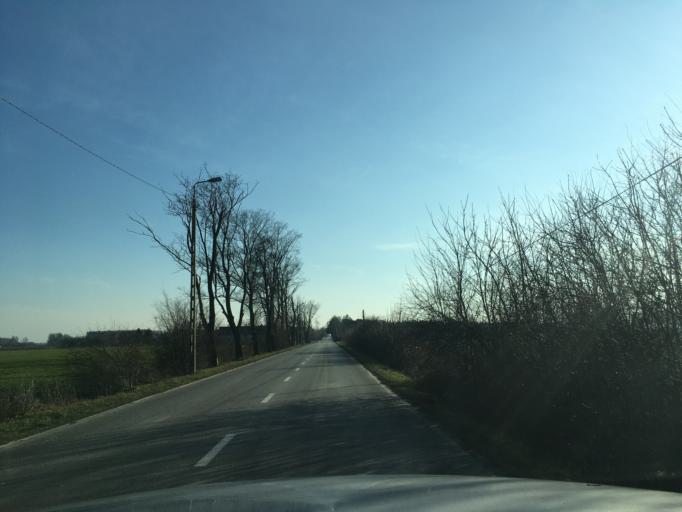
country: PL
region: Masovian Voivodeship
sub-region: Powiat pruszkowski
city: Nadarzyn
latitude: 52.0516
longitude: 20.8253
